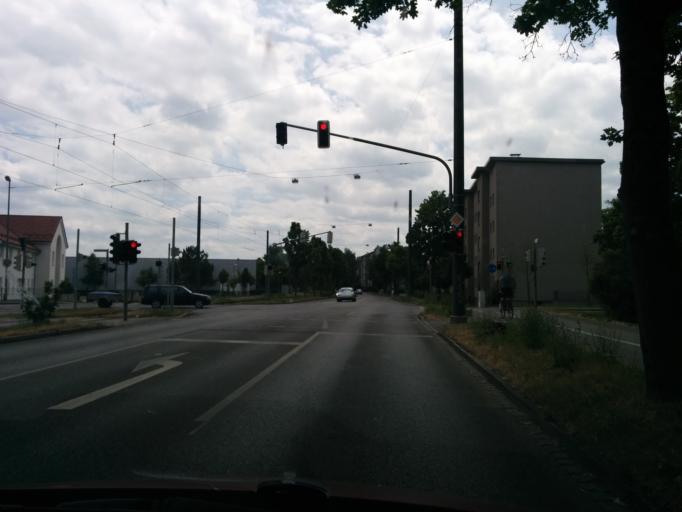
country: DE
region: Bavaria
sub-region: Swabia
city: Augsburg
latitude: 48.3464
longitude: 10.9002
